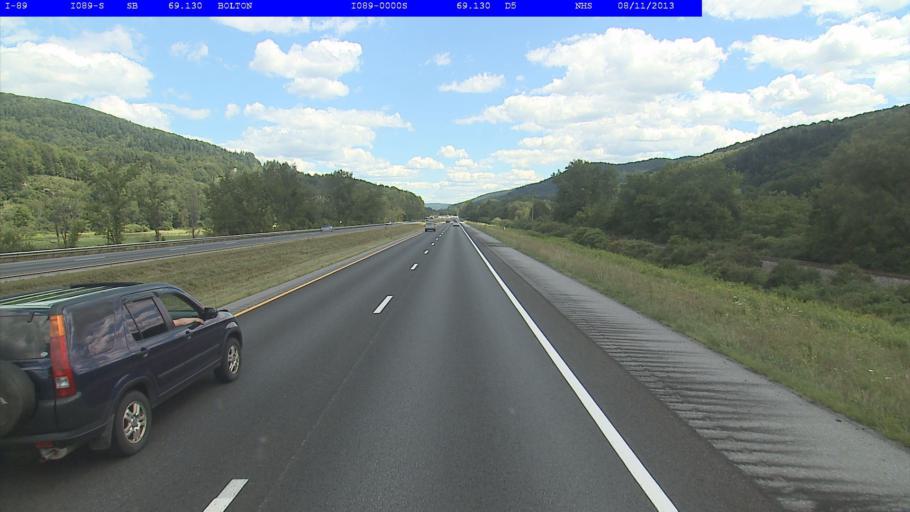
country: US
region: Vermont
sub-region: Washington County
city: Waterbury
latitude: 44.3654
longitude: -72.8518
